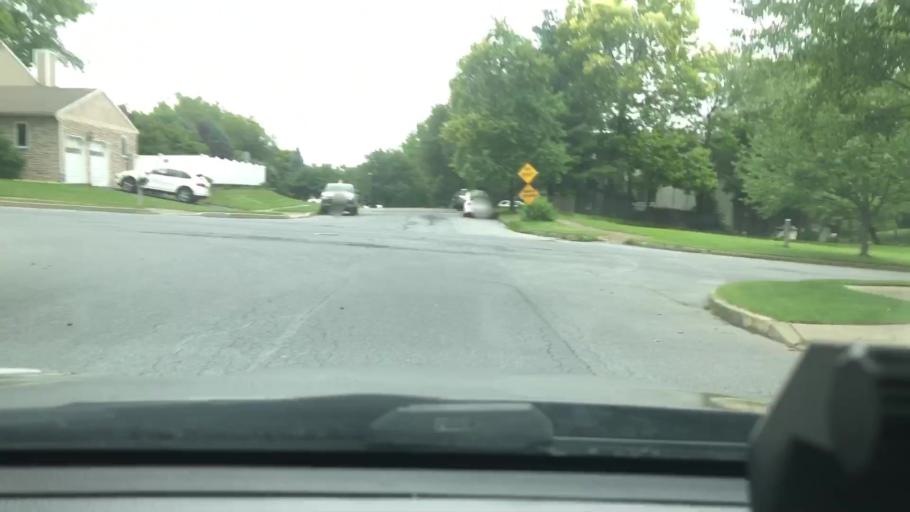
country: US
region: Pennsylvania
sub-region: Lehigh County
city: Allentown
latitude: 40.6188
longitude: -75.4903
